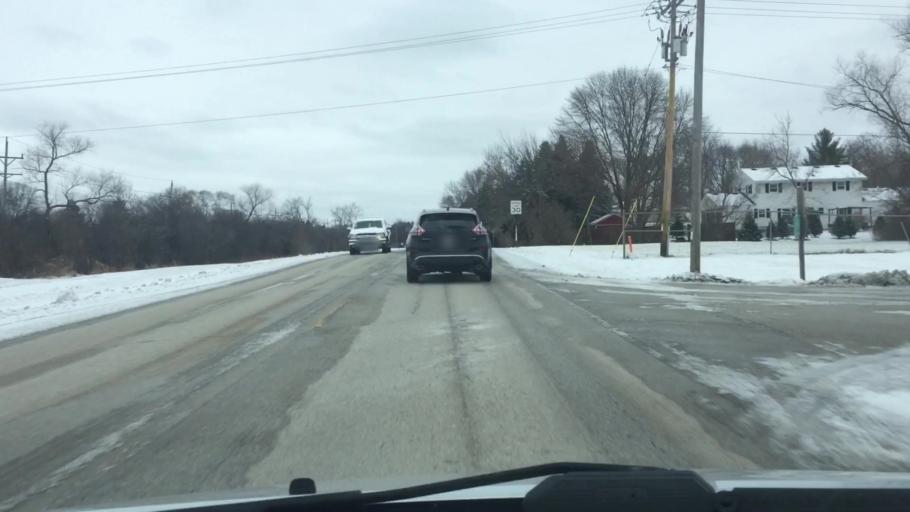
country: US
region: Wisconsin
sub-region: Waukesha County
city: Brookfield
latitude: 43.0497
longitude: -88.1059
